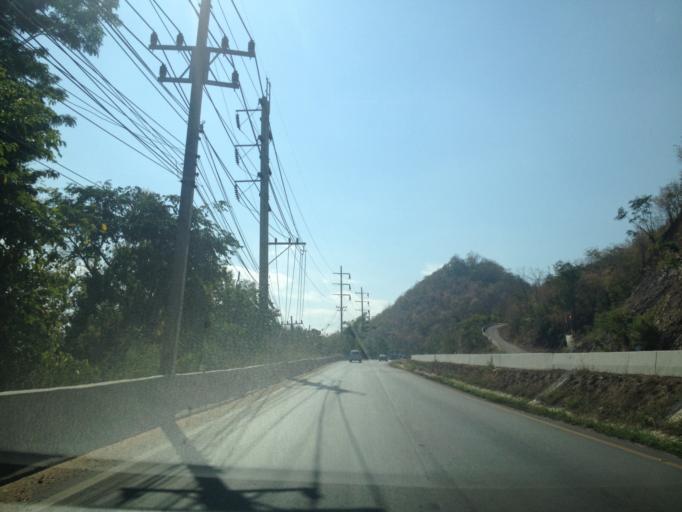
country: TH
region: Chiang Mai
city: Chom Thong
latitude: 18.3795
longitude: 98.6798
